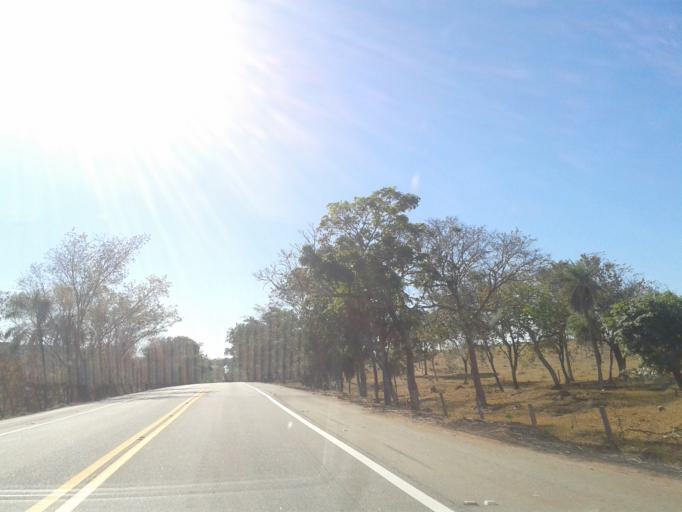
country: BR
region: Goias
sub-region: Itapuranga
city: Itapuranga
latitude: -15.6058
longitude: -50.2511
